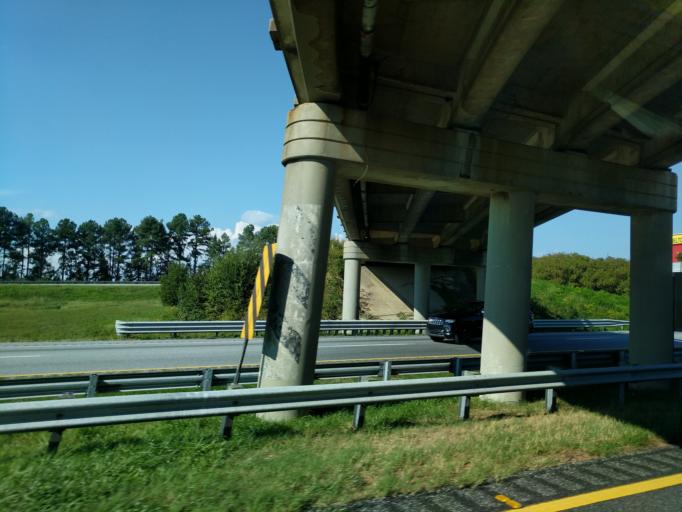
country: US
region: Georgia
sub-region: Hart County
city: Reed Creek
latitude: 34.5001
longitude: -82.9946
